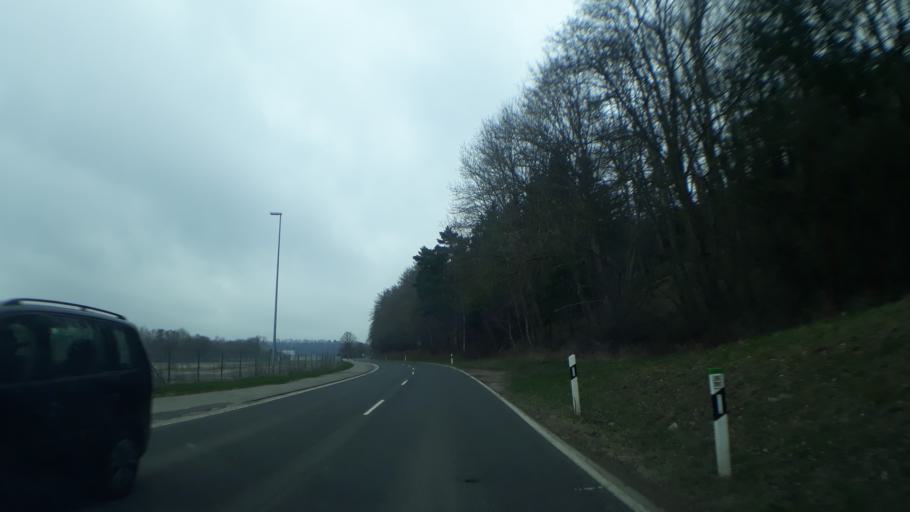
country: DE
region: North Rhine-Westphalia
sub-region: Regierungsbezirk Koln
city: Kall
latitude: 50.5308
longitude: 6.5536
